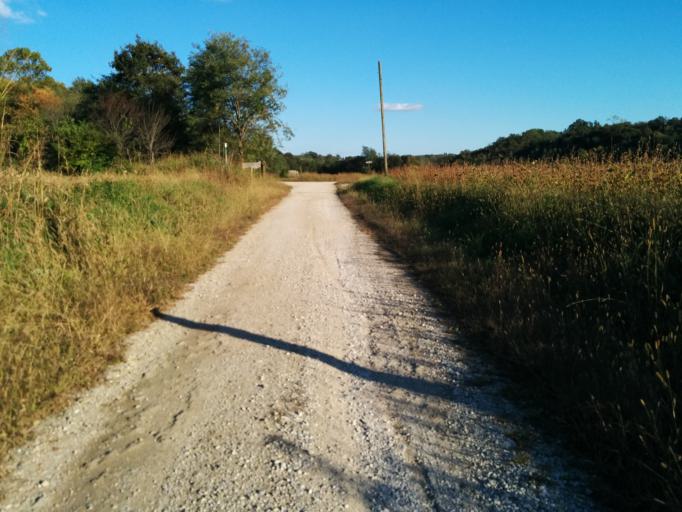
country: IT
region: Friuli Venezia Giulia
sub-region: Provincia di Udine
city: Cassacco
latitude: 46.1557
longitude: 13.1715
